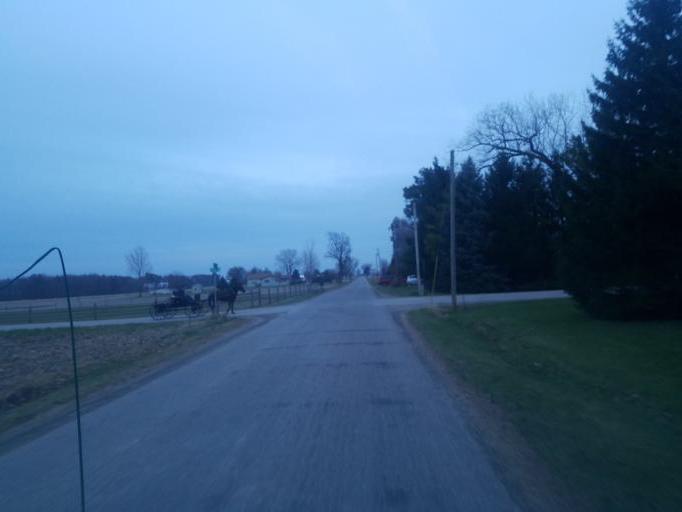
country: US
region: Indiana
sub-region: Adams County
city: Decatur
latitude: 40.7588
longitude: -84.9956
